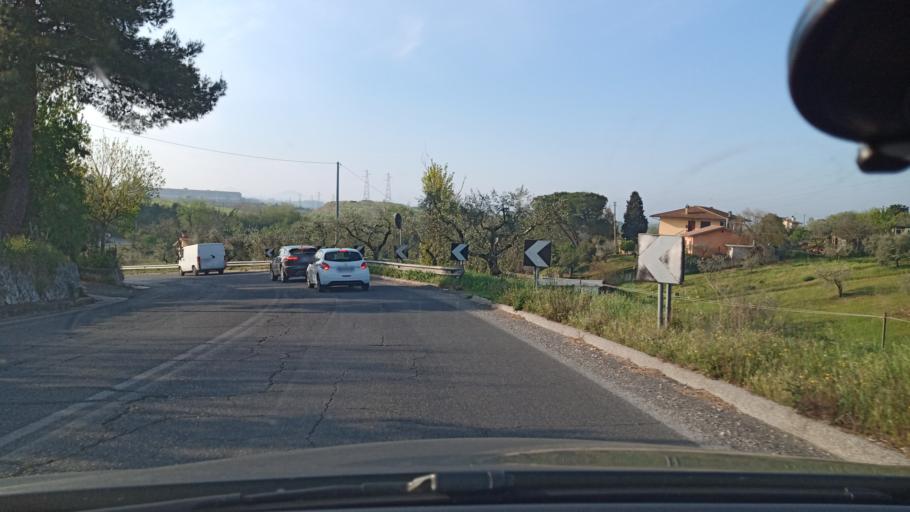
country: IT
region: Latium
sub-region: Citta metropolitana di Roma Capitale
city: Fiano Romano
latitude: 42.1791
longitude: 12.6359
